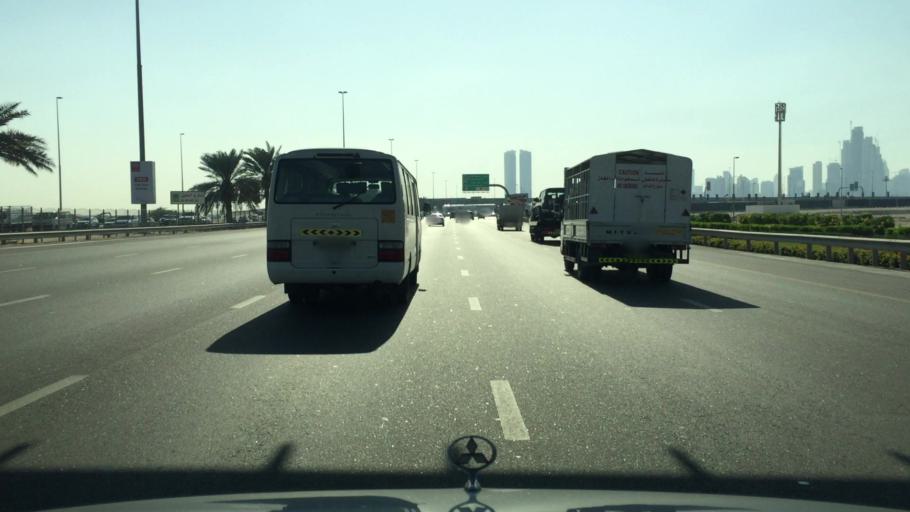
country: AE
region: Ash Shariqah
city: Sharjah
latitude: 25.2107
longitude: 55.3194
